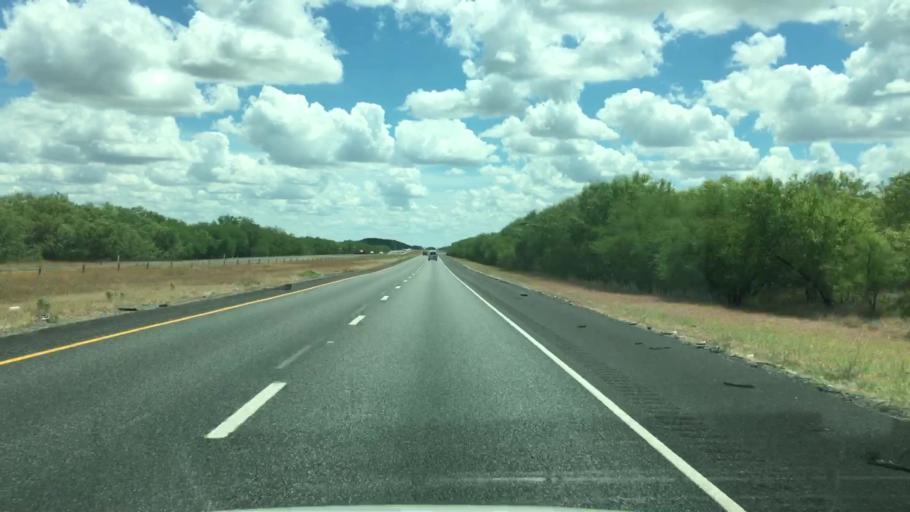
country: US
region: Texas
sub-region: Atascosa County
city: Pleasanton
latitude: 28.7449
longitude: -98.2933
